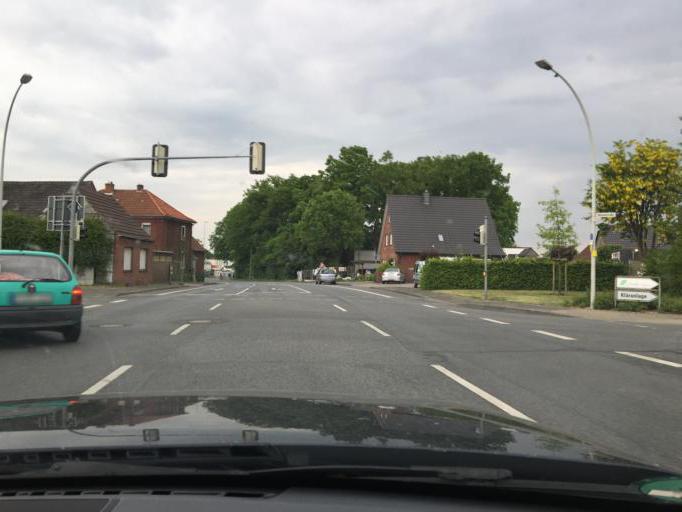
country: DE
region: North Rhine-Westphalia
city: Emsdetten
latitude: 52.1730
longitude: 7.5381
